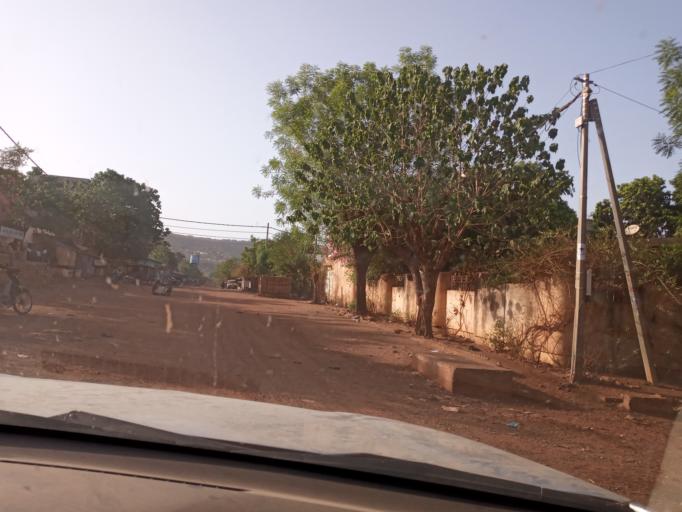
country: ML
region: Bamako
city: Bamako
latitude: 12.6691
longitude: -7.9750
